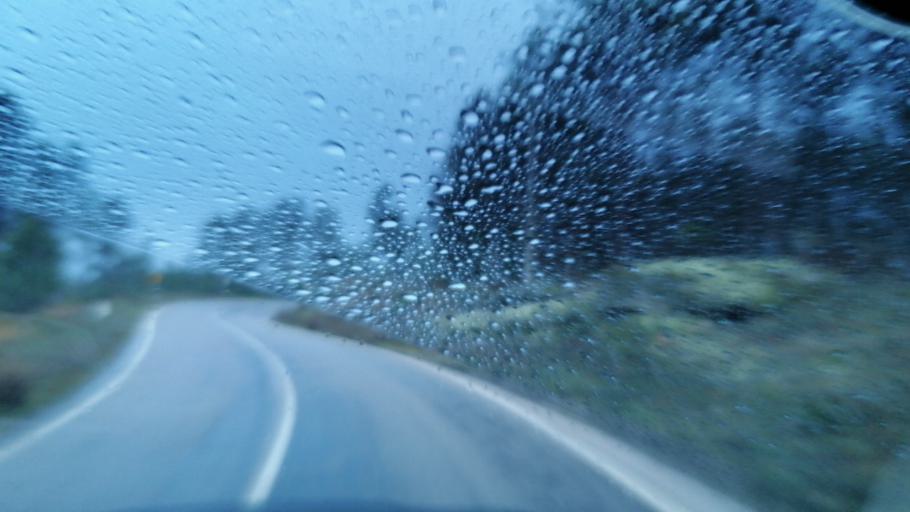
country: PT
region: Vila Real
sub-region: Murca
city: Murca
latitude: 41.4271
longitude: -7.5059
